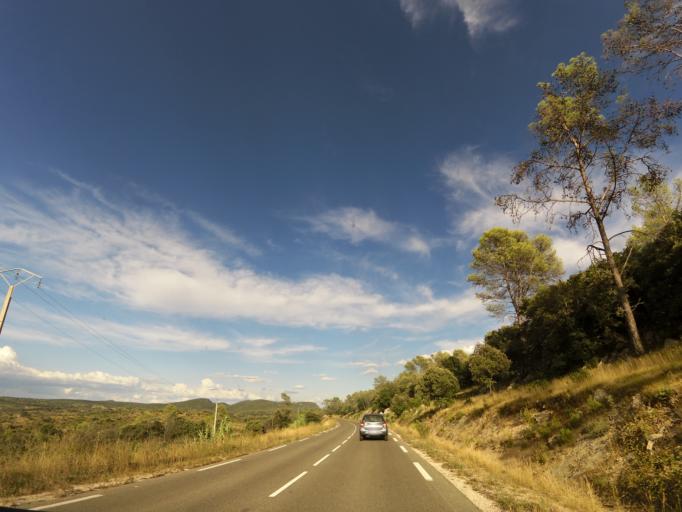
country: FR
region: Languedoc-Roussillon
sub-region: Departement de l'Herault
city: Saint-Mathieu-de-Treviers
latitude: 43.7806
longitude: 3.9257
